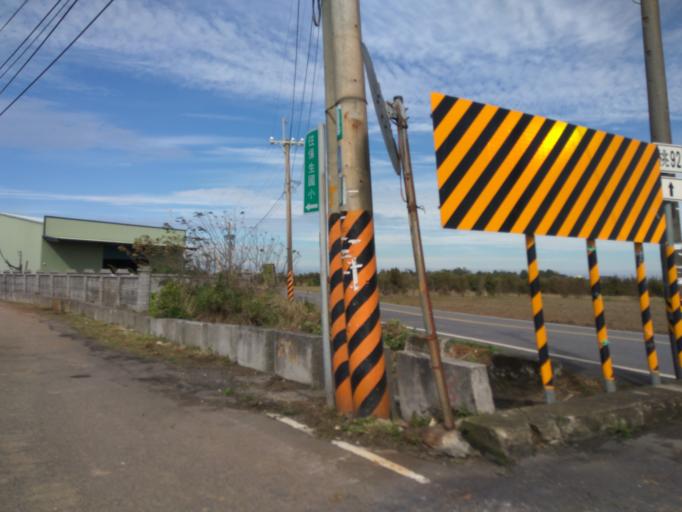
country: TW
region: Taiwan
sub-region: Hsinchu
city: Zhubei
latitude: 25.0056
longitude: 121.0799
